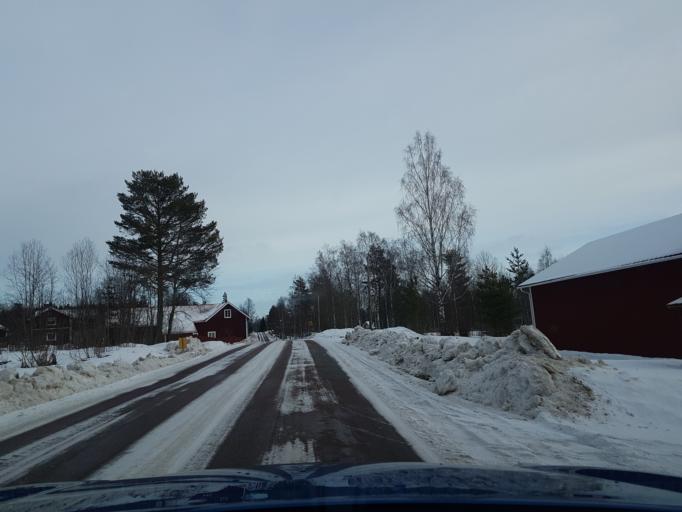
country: SE
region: Dalarna
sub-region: Leksand Municipality
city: Leksand
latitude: 60.7503
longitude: 15.0097
